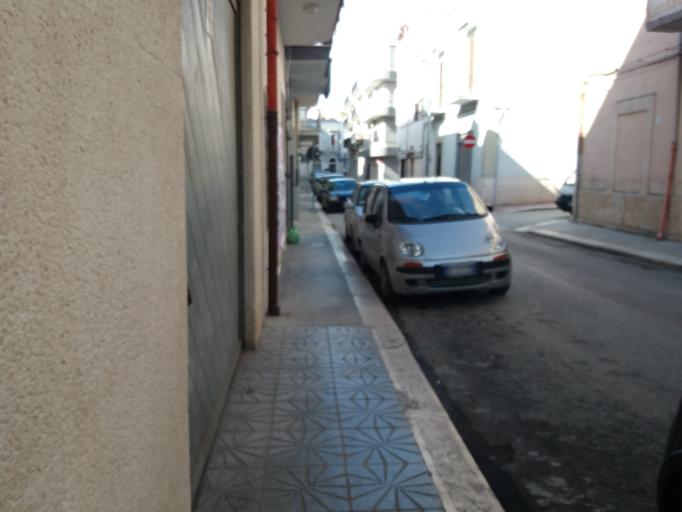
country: IT
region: Apulia
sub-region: Provincia di Barletta - Andria - Trani
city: Andria
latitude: 41.2228
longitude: 16.3013
